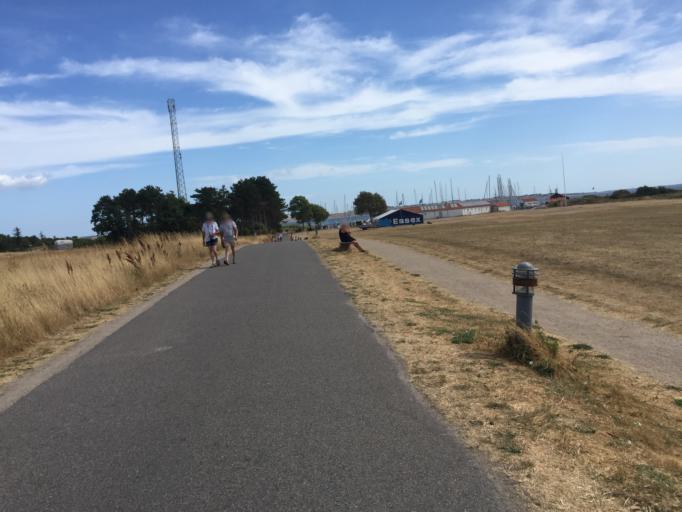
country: DK
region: Central Jutland
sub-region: Samso Kommune
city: Tranebjerg
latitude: 55.9490
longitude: 10.4482
